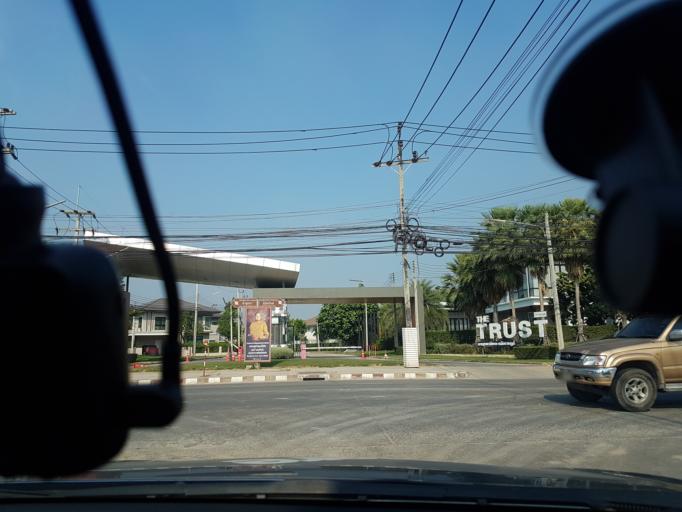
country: TH
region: Pathum Thani
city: Lam Luk Ka
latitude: 13.9175
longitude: 100.7176
